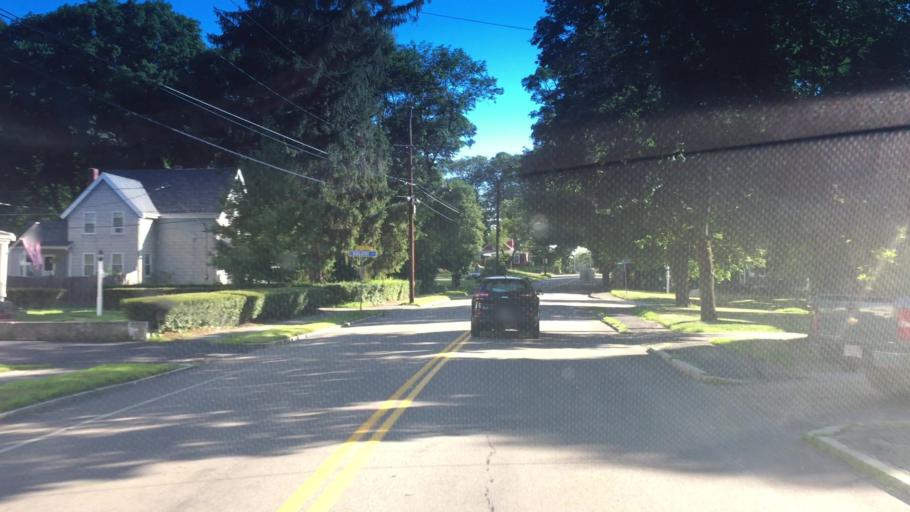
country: US
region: Massachusetts
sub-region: Norfolk County
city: Norwood
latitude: 42.1626
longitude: -71.2095
